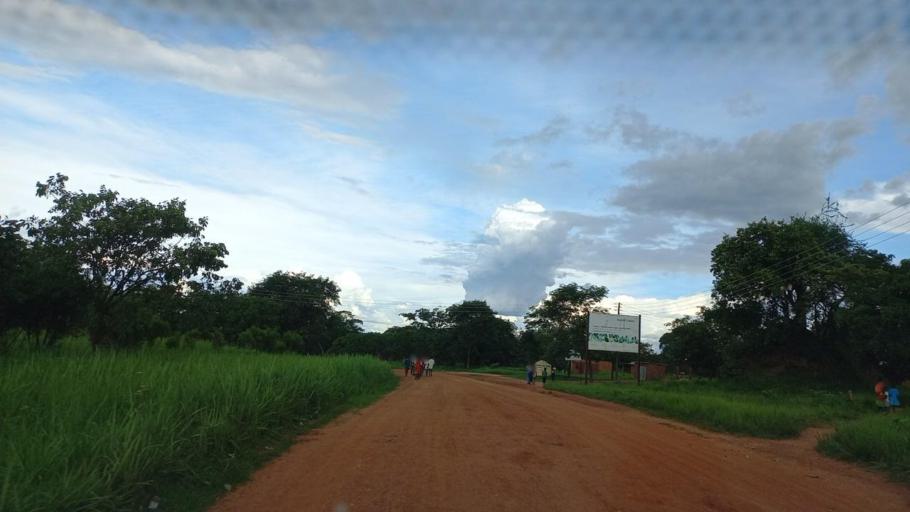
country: ZM
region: North-Western
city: Mwinilunga
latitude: -11.7587
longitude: 24.4278
